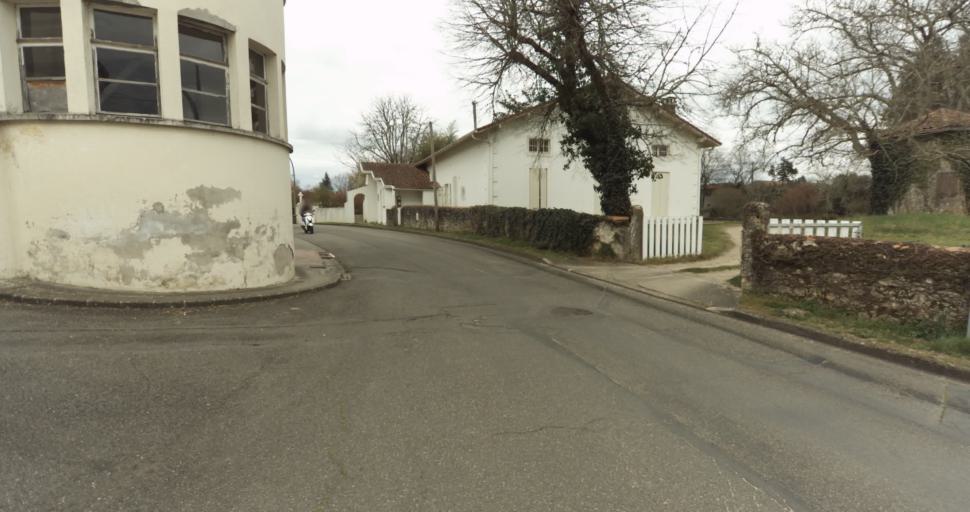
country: FR
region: Aquitaine
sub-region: Departement des Landes
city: Roquefort
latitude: 44.0324
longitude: -0.3209
